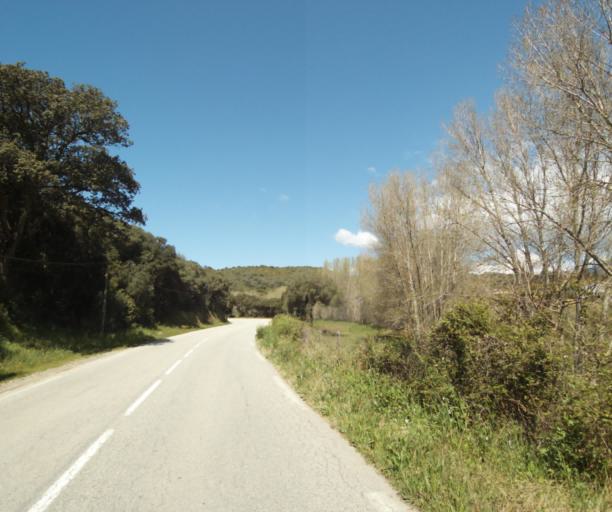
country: FR
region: Corsica
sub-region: Departement de la Corse-du-Sud
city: Propriano
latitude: 41.6585
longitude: 8.9150
